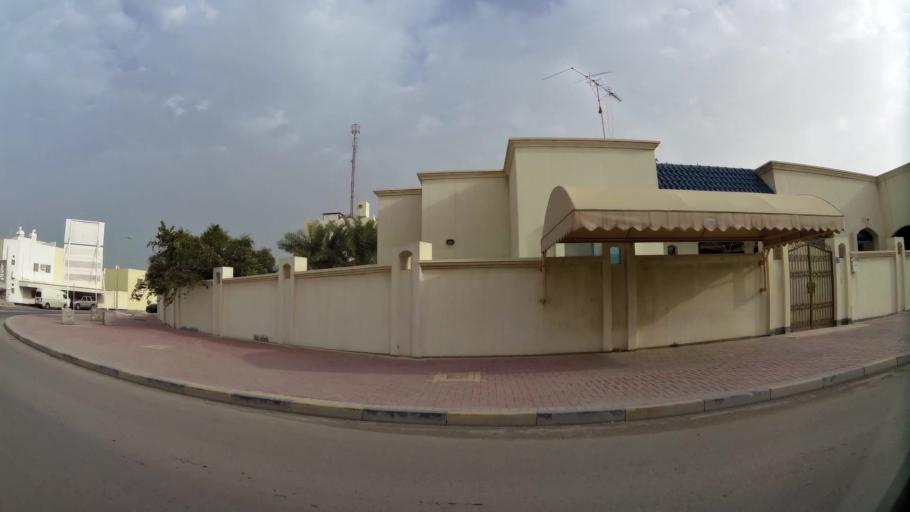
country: BH
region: Northern
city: Ar Rifa'
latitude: 26.1426
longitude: 50.5671
